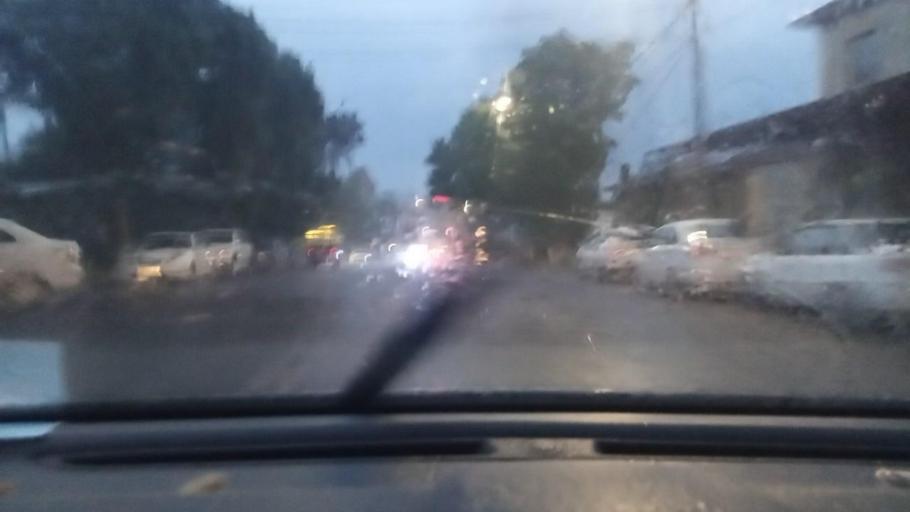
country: UZ
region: Toshkent
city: Salor
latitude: 41.3261
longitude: 69.3489
